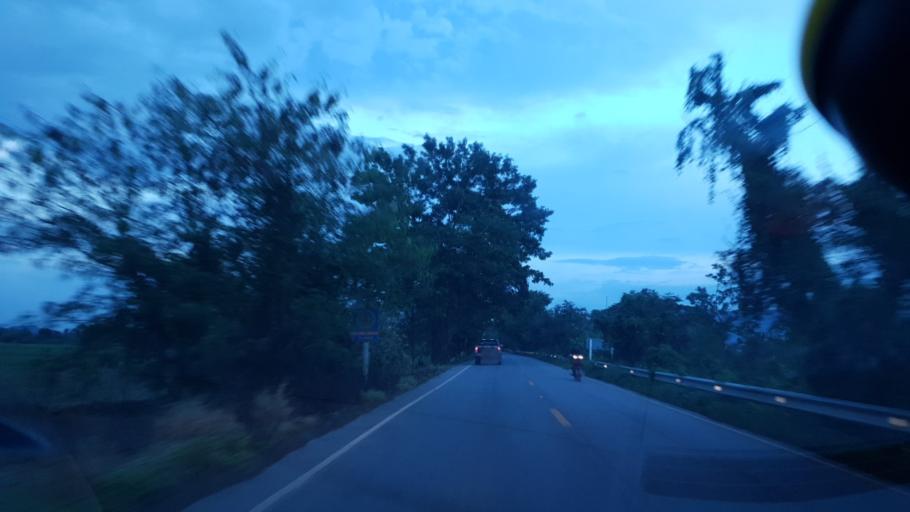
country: TH
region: Chiang Rai
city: Wiang Chai
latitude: 19.9711
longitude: 99.9701
